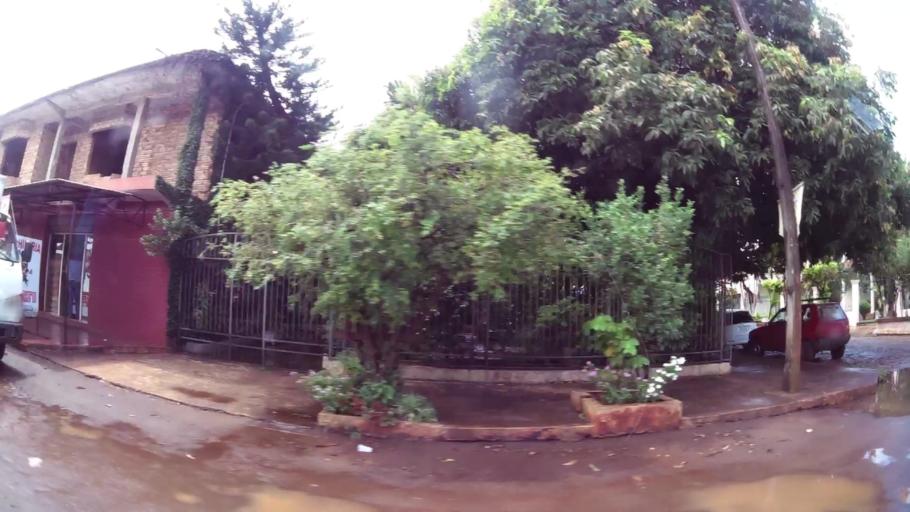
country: PY
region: Alto Parana
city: Ciudad del Este
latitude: -25.5047
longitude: -54.6667
